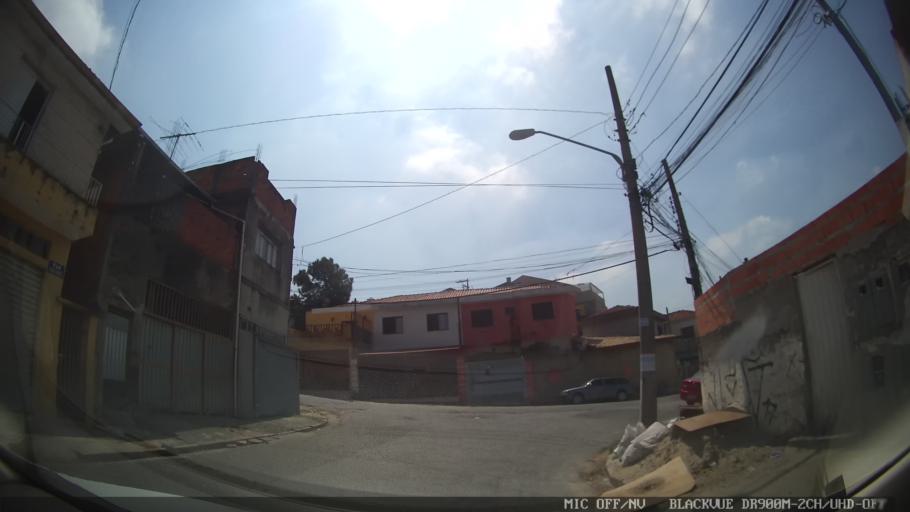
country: BR
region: Sao Paulo
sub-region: Sao Paulo
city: Sao Paulo
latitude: -23.4996
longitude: -46.6663
